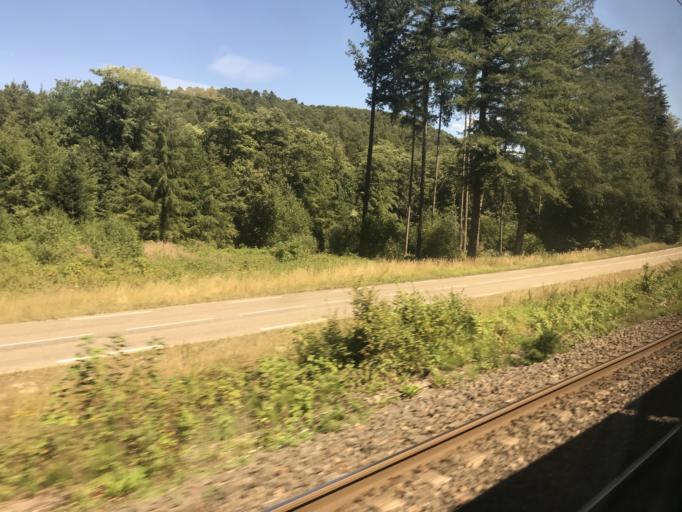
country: FR
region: Lorraine
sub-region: Departement de la Moselle
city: Phalsbourg
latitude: 48.7335
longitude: 7.2781
